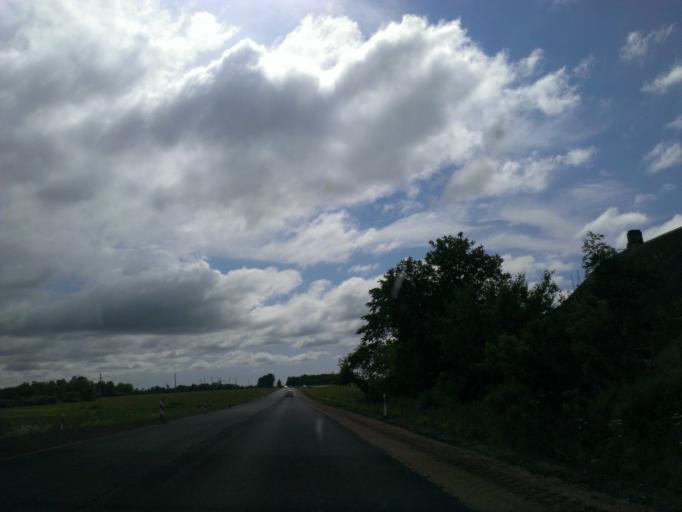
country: LV
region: Durbe
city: Liegi
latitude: 56.5720
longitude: 21.2842
